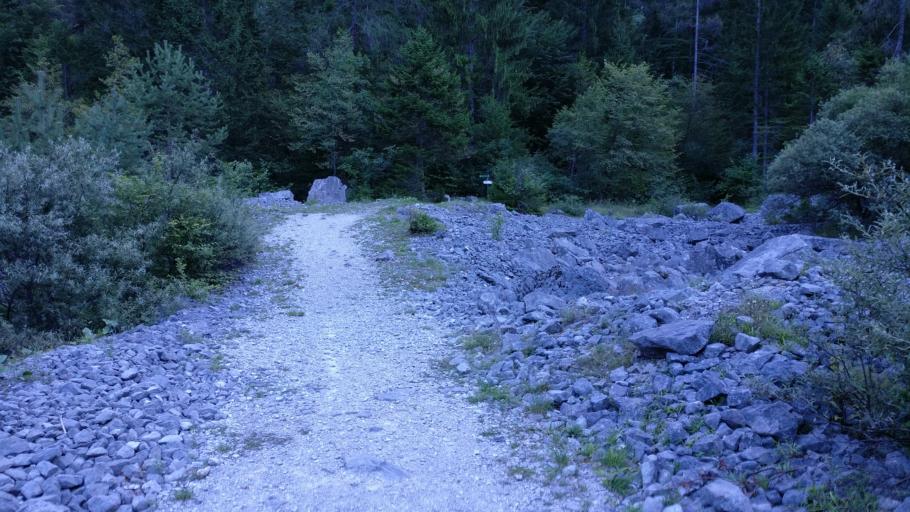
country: IT
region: Trentino-Alto Adige
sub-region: Provincia di Trento
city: Terres
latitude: 46.2899
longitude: 10.9747
